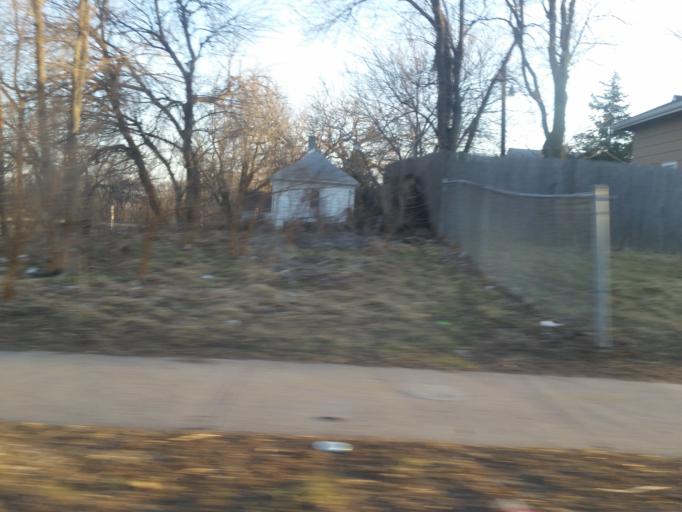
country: US
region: Nebraska
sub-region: Douglas County
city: Omaha
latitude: 41.2342
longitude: -95.9281
